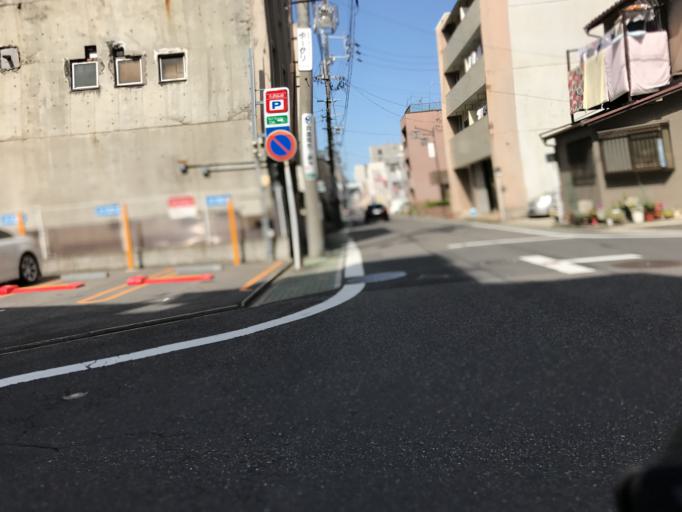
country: JP
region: Aichi
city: Nagoya-shi
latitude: 35.1779
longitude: 136.9201
